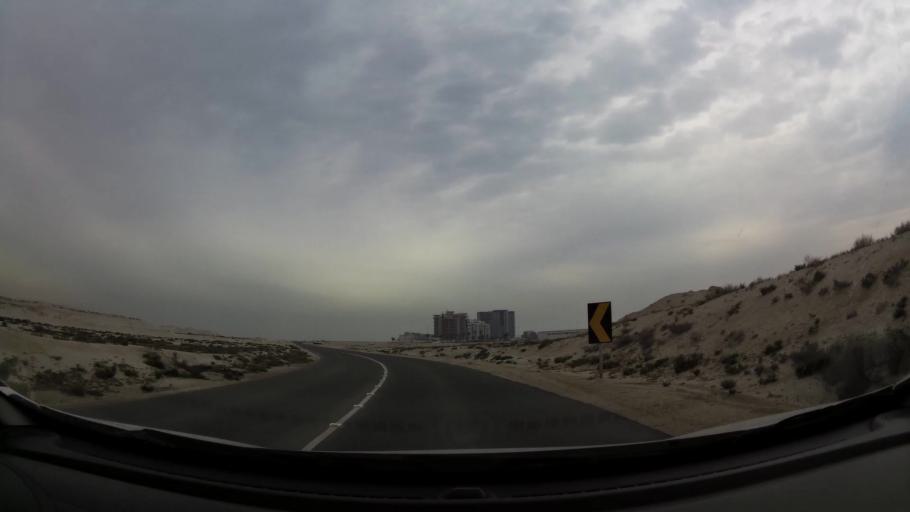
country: BH
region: Central Governorate
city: Dar Kulayb
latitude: 25.8677
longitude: 50.6032
